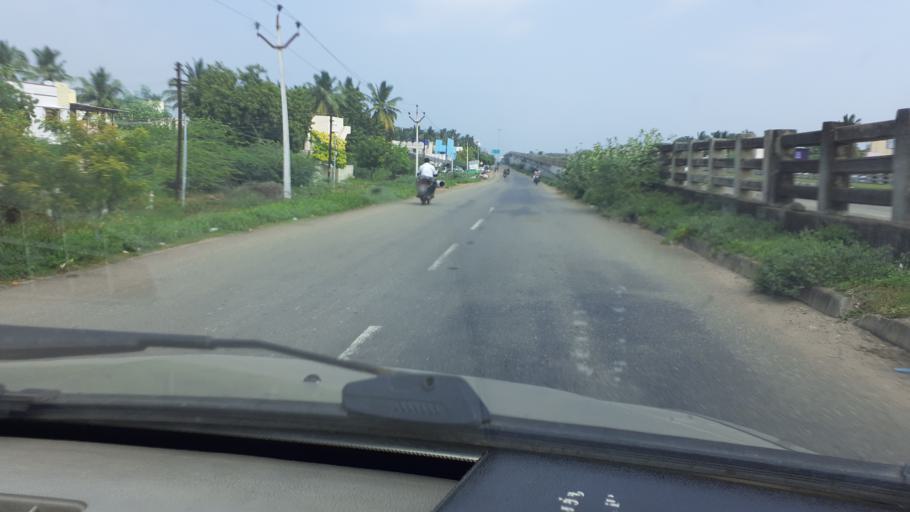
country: IN
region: Tamil Nadu
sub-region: Tirunelveli Kattabo
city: Tirunelveli
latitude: 8.7091
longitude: 77.7653
